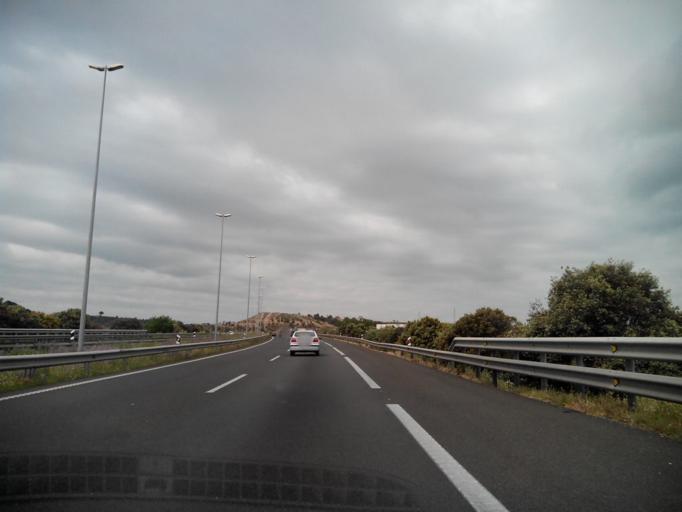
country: ES
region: Catalonia
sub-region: Provincia de Lleida
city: Tarrega
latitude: 41.6617
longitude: 1.1382
